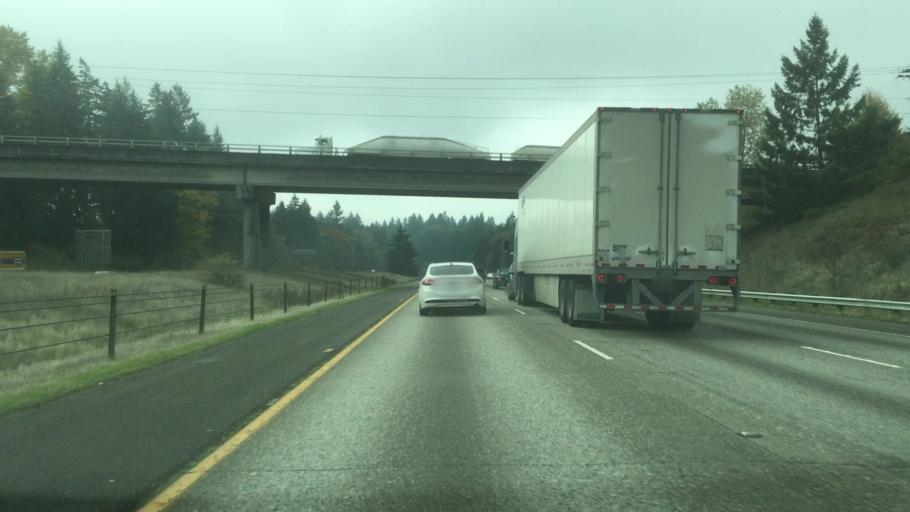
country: US
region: Washington
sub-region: Thurston County
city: Tanglewilde-Thompson Place
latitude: 47.0586
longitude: -122.7964
